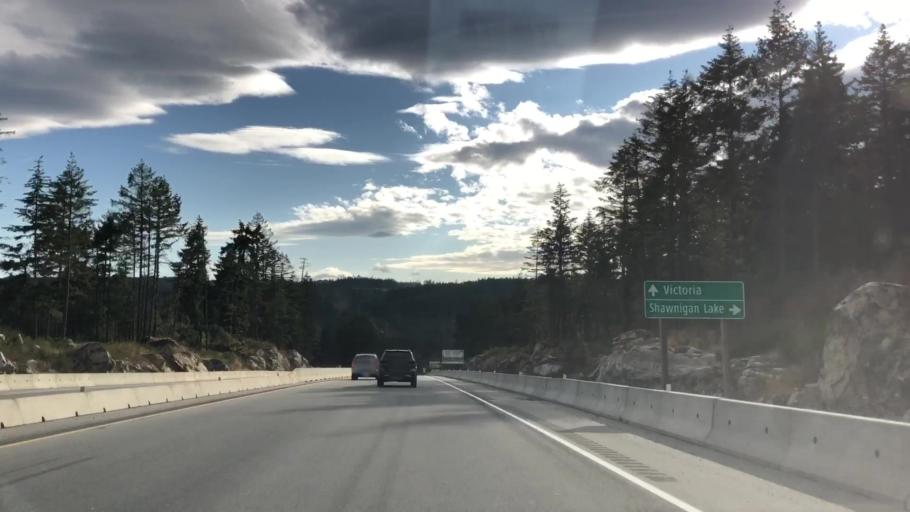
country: CA
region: British Columbia
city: Langford
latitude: 48.5651
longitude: -123.5636
